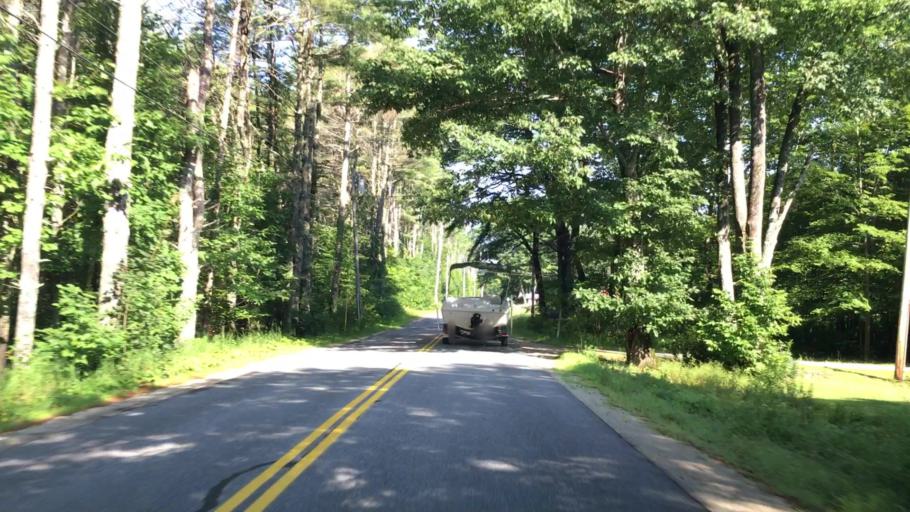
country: US
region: Maine
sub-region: Androscoggin County
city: Poland
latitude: 44.0580
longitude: -70.3820
